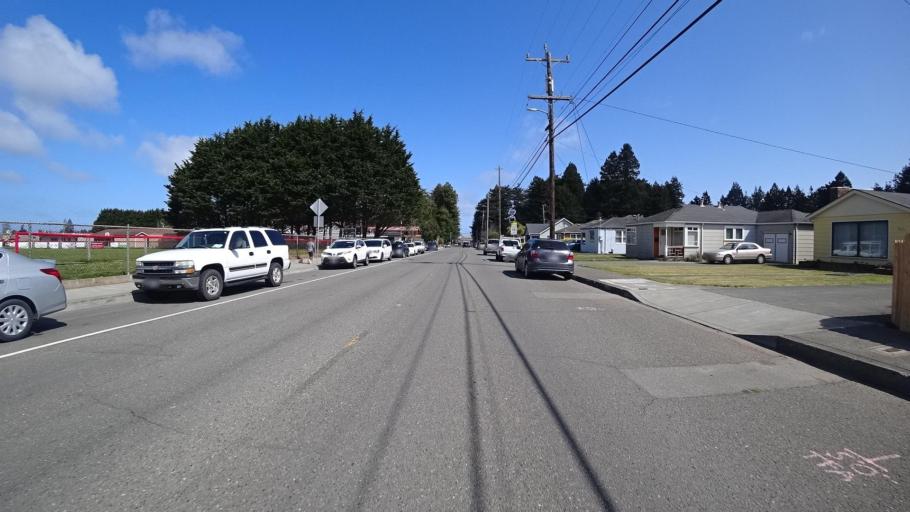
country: US
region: California
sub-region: Humboldt County
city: Cutten
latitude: 40.7772
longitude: -124.1421
